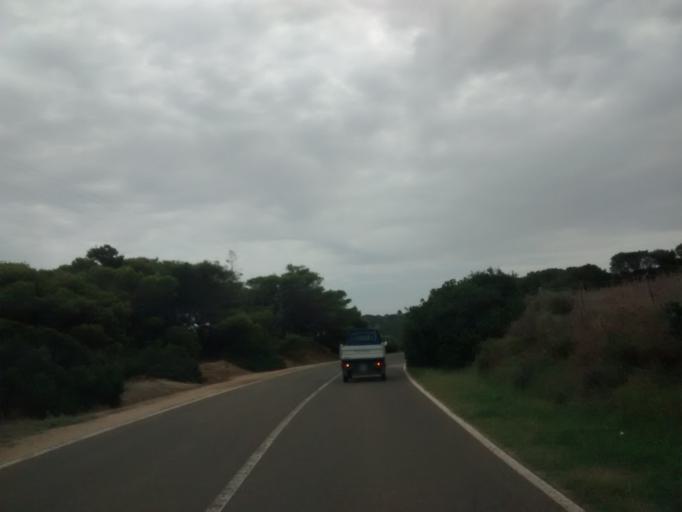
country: IT
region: Sardinia
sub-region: Provincia di Cagliari
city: Villasimius
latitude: 39.1127
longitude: 9.5103
